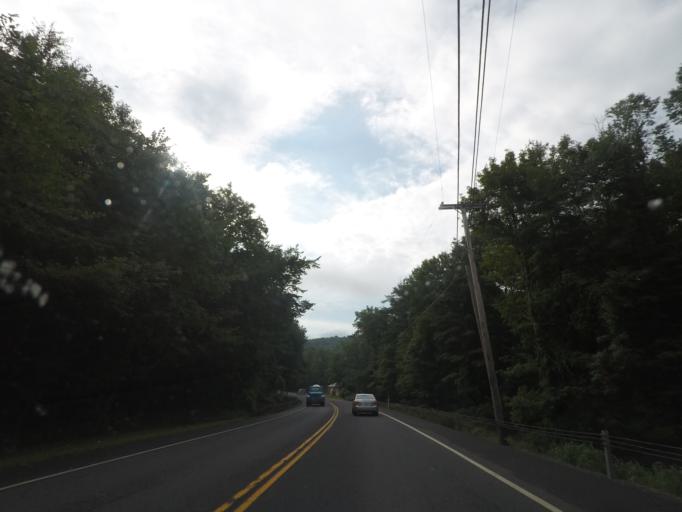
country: US
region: New York
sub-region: Rensselaer County
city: Nassau
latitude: 42.4956
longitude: -73.5525
